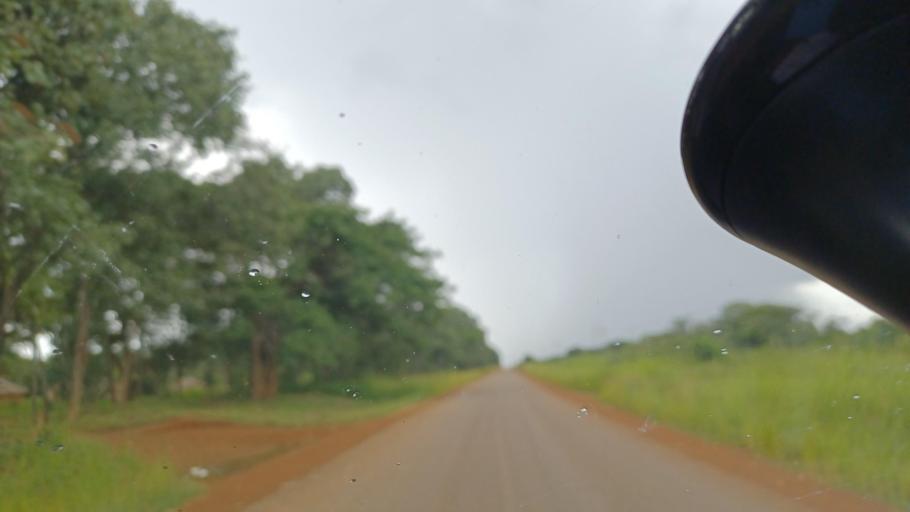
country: ZM
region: North-Western
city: Kasempa
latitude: -13.0467
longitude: 25.9912
